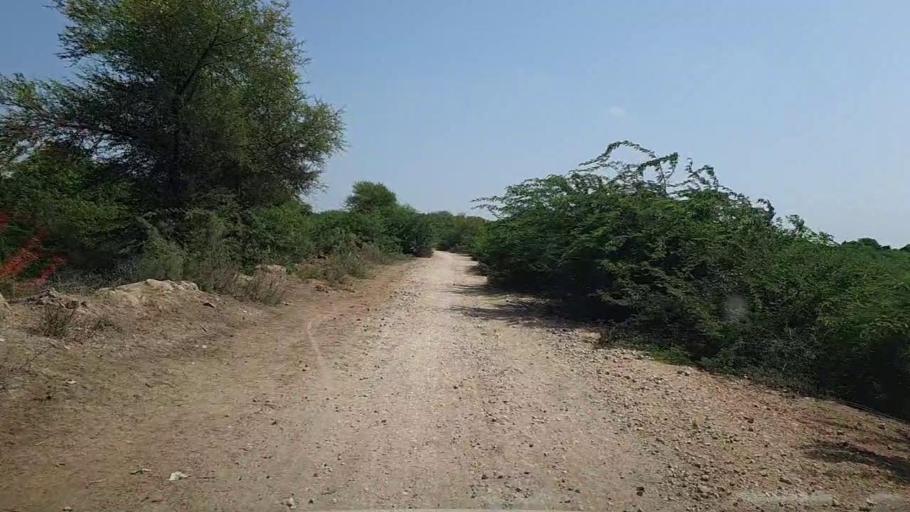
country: PK
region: Sindh
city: Kario
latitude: 24.8375
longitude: 68.7079
